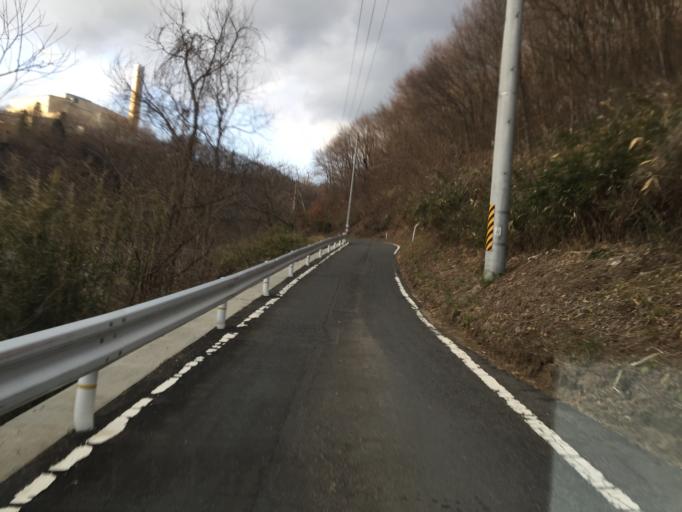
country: JP
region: Fukushima
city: Motomiya
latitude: 37.5292
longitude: 140.4152
